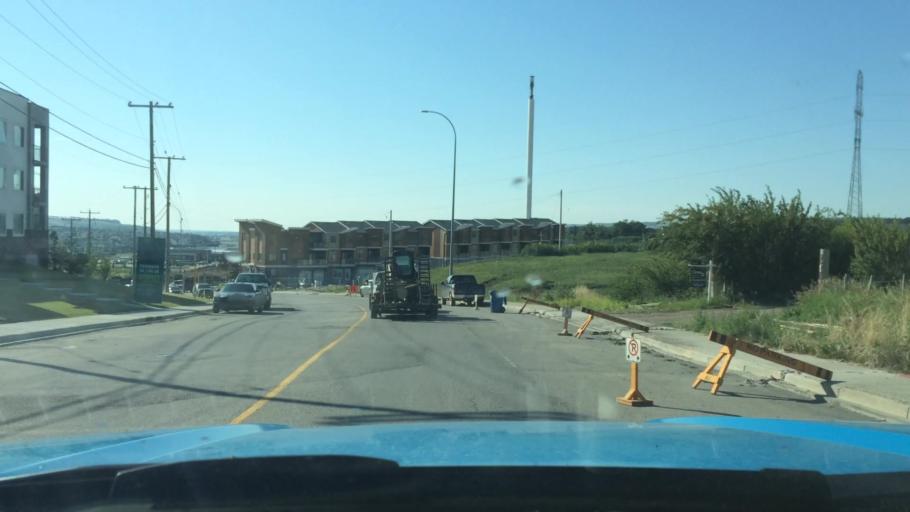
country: CA
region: Alberta
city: Calgary
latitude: 51.1706
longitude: -114.1367
